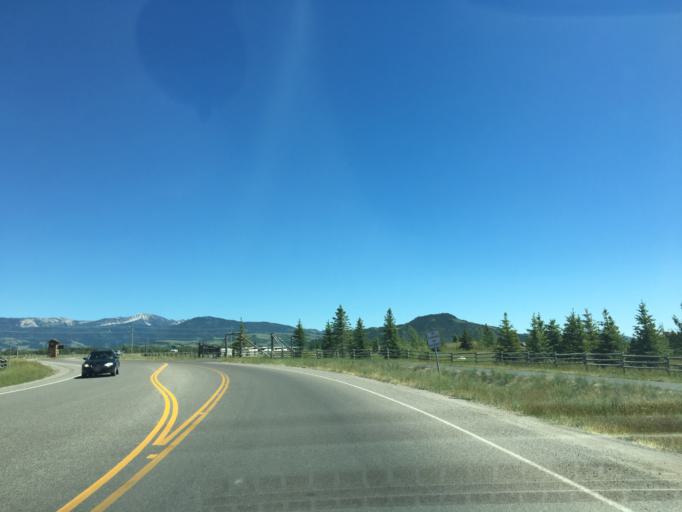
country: US
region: Wyoming
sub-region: Teton County
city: Moose Wilson Road
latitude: 43.5849
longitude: -110.8257
